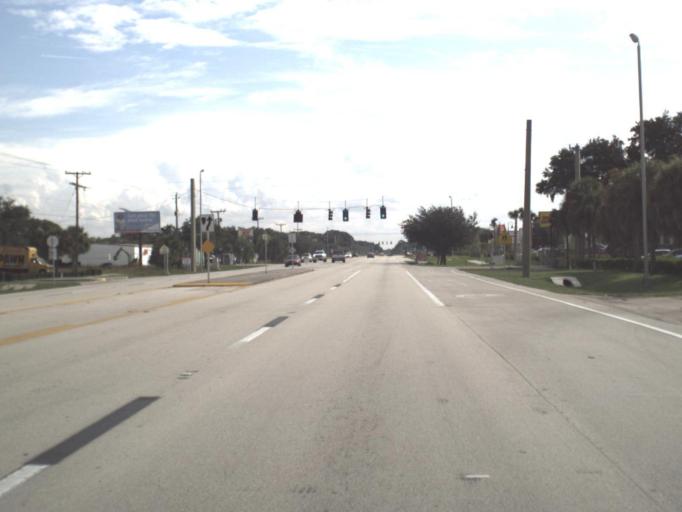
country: US
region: Florida
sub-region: Lee County
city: Olga
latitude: 26.7088
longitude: -81.7258
